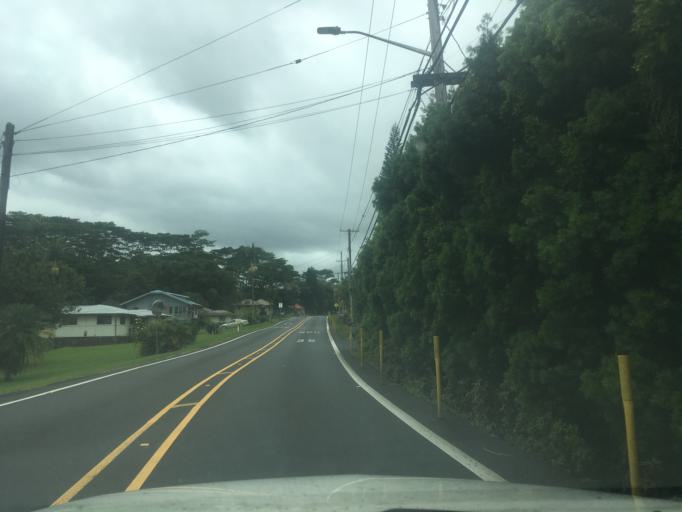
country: US
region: Hawaii
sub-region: Hawaii County
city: Hilo
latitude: 19.6955
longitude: -155.1190
